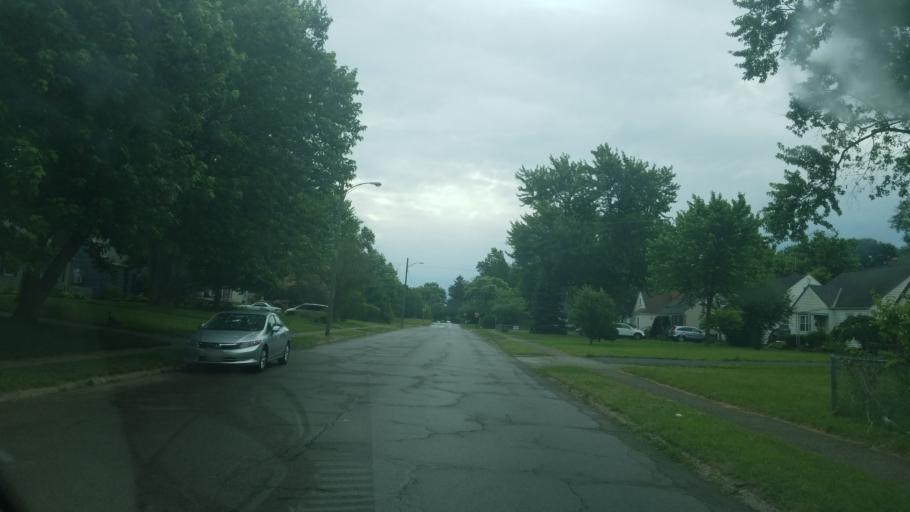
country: US
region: Ohio
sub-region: Franklin County
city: Minerva Park
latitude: 40.0302
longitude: -82.9794
